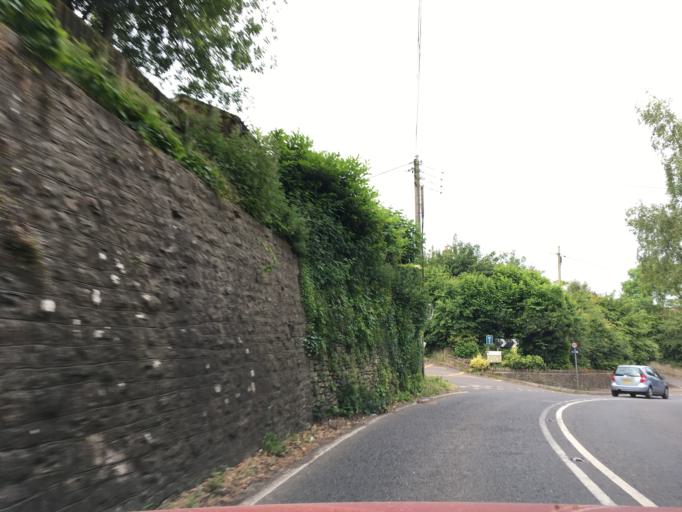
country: GB
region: England
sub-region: North Somerset
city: Portishead
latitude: 51.4627
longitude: -2.7558
